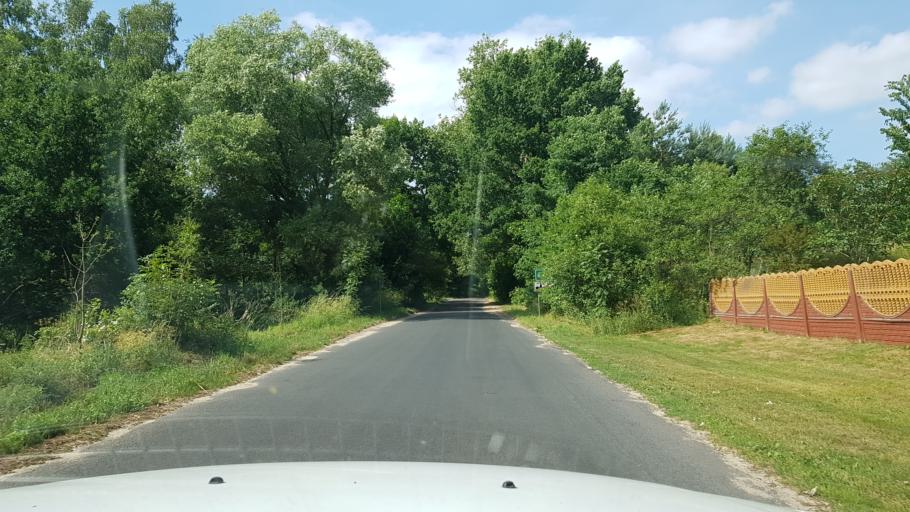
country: PL
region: West Pomeranian Voivodeship
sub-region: Powiat goleniowski
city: Mosty
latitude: 53.5657
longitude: 14.9747
